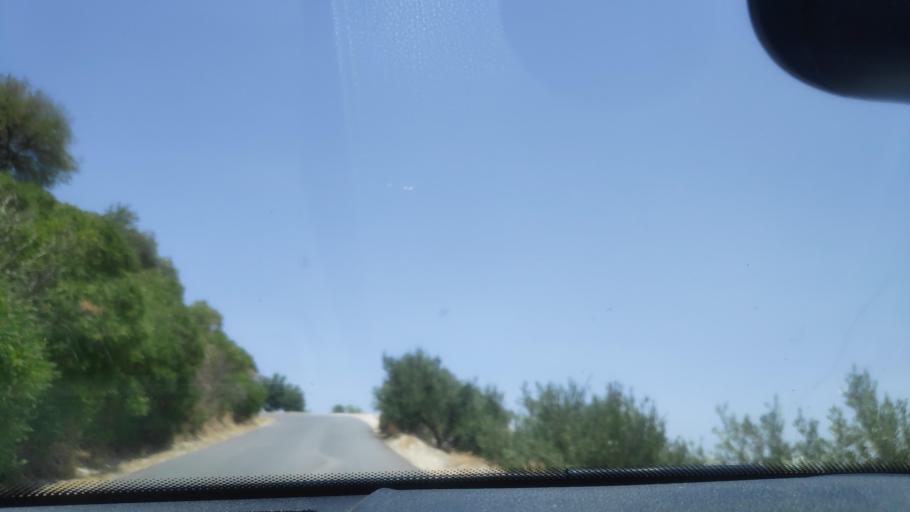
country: ES
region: Andalusia
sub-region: Provincia de Jaen
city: Torres
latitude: 37.7918
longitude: -3.4620
